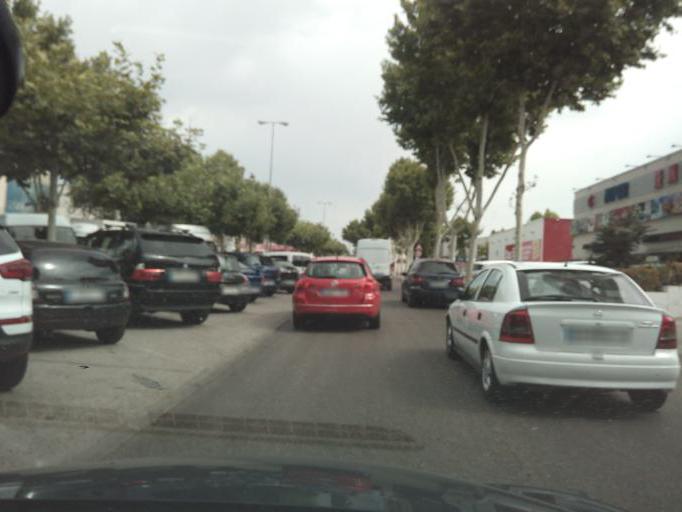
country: ES
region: Madrid
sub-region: Provincia de Madrid
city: Las Rozas de Madrid
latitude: 40.5008
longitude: -3.8892
